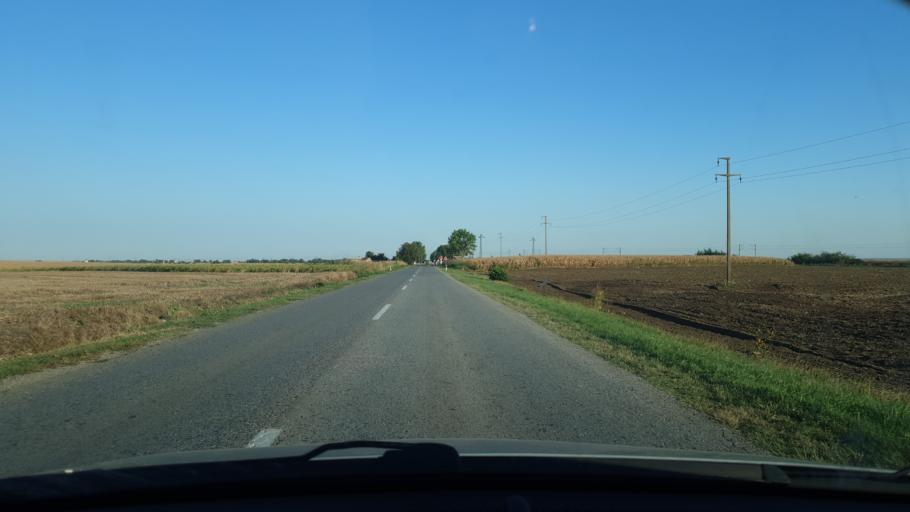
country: RS
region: Autonomna Pokrajina Vojvodina
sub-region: Sremski Okrug
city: Ruma
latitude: 44.9912
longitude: 19.8588
